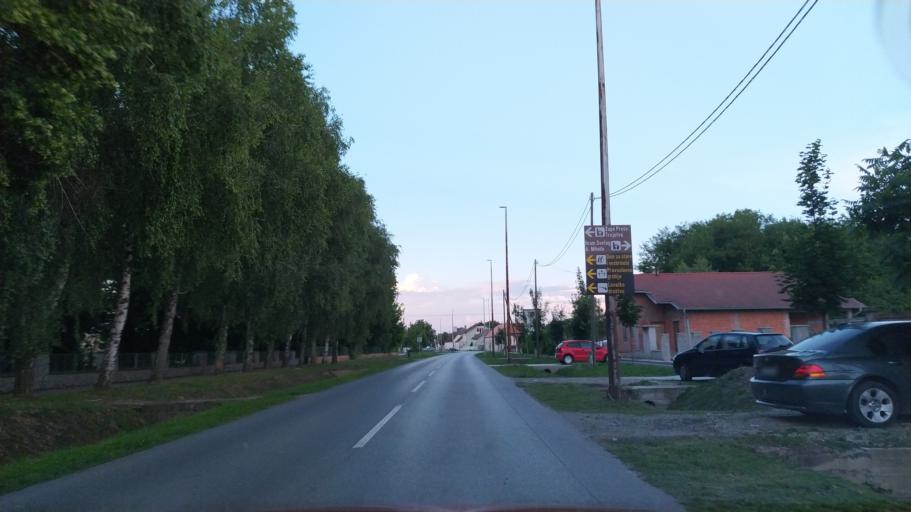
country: HR
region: Osjecko-Baranjska
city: Cepin
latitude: 45.5182
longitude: 18.5510
